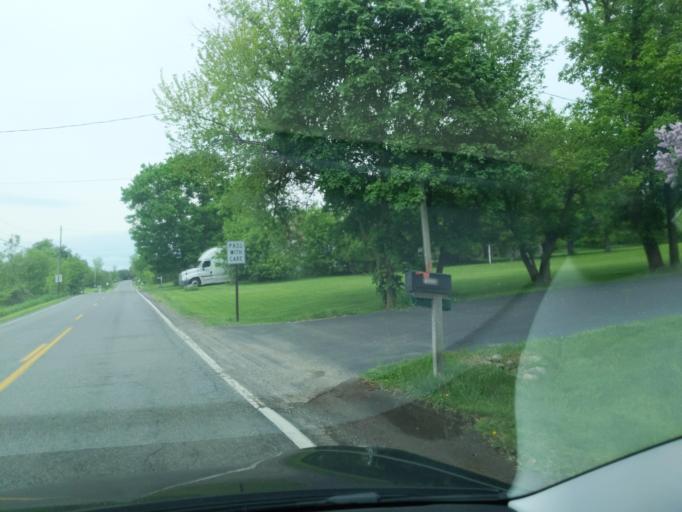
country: US
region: Michigan
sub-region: Ingham County
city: Mason
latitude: 42.5270
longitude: -84.4281
